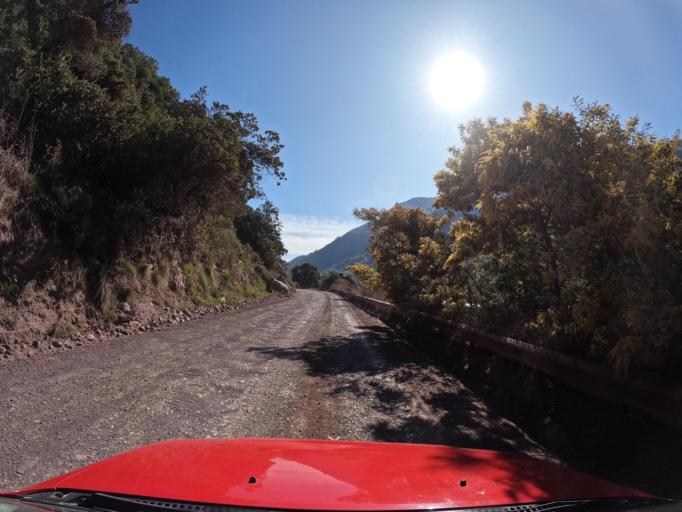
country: CL
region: O'Higgins
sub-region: Provincia de Colchagua
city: Chimbarongo
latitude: -34.9999
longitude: -70.7818
